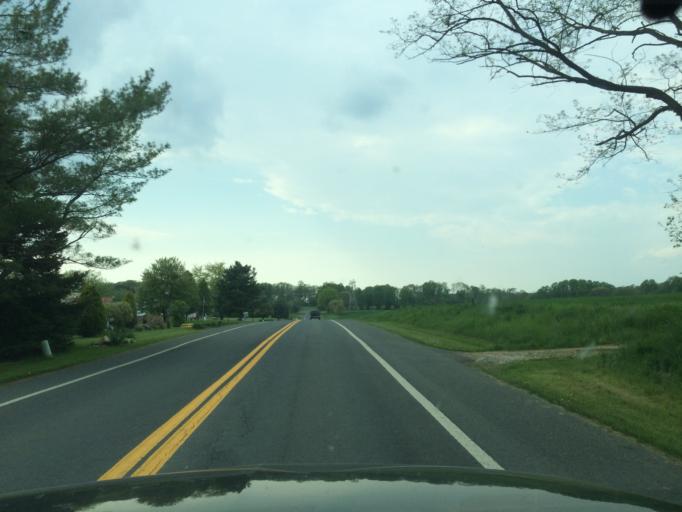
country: US
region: Maryland
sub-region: Carroll County
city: Sykesville
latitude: 39.3969
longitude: -77.0290
